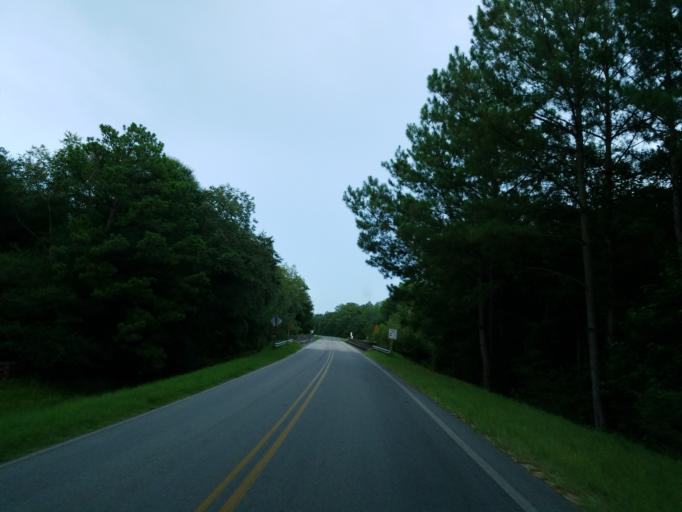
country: US
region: Georgia
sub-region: Cook County
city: Sparks
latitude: 31.2542
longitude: -83.5094
